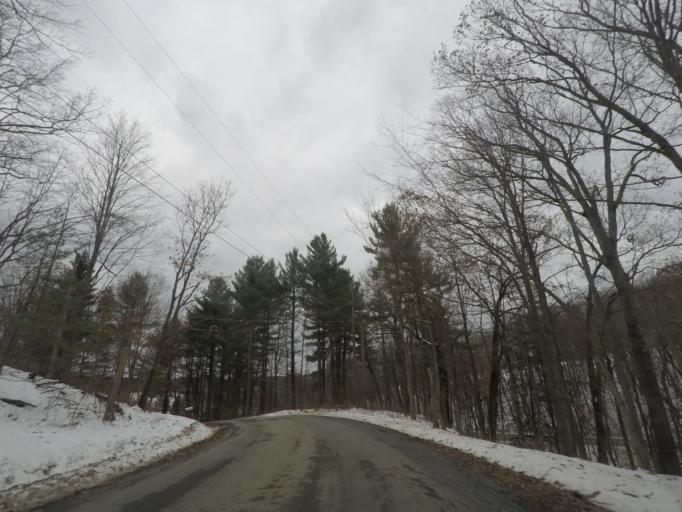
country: US
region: New York
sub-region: Rensselaer County
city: West Sand Lake
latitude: 42.6131
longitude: -73.6316
